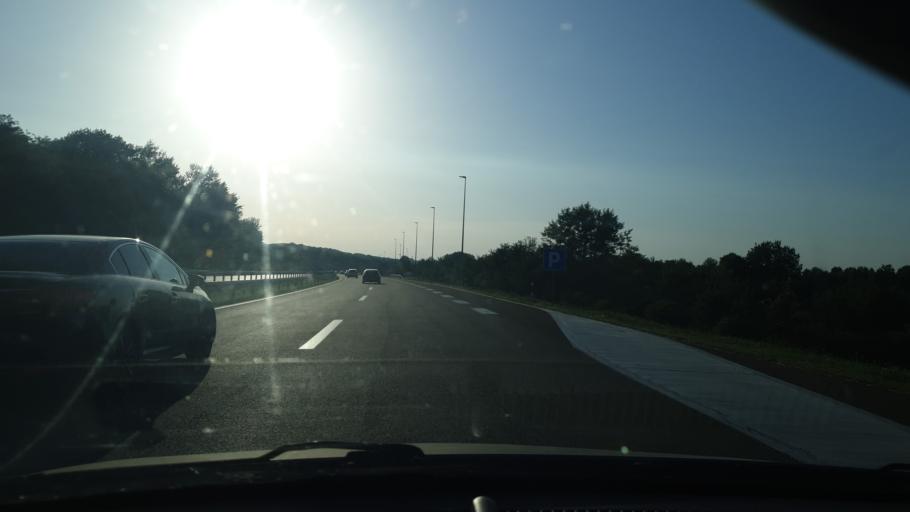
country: RS
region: Central Serbia
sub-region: Podunavski Okrug
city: Smederevo
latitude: 44.5753
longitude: 20.9051
